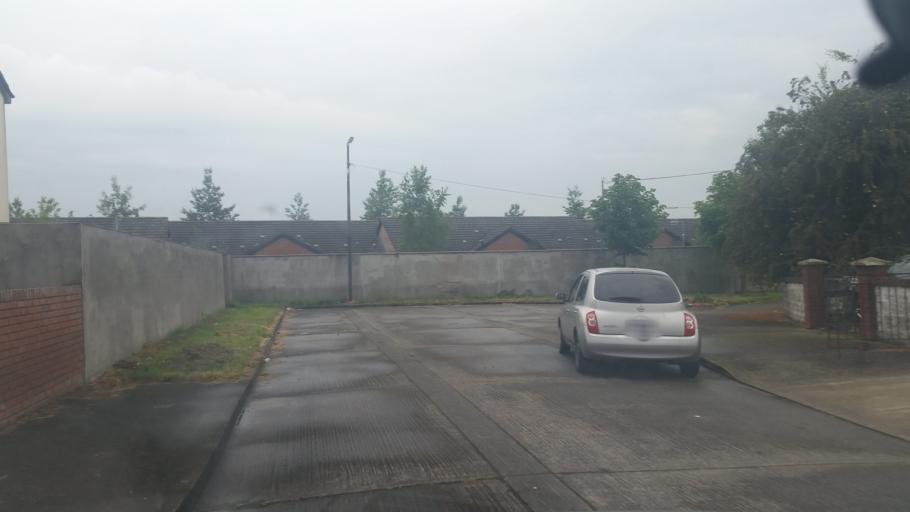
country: IE
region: Leinster
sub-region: Dublin City
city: Finglas
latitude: 53.3865
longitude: -6.3182
